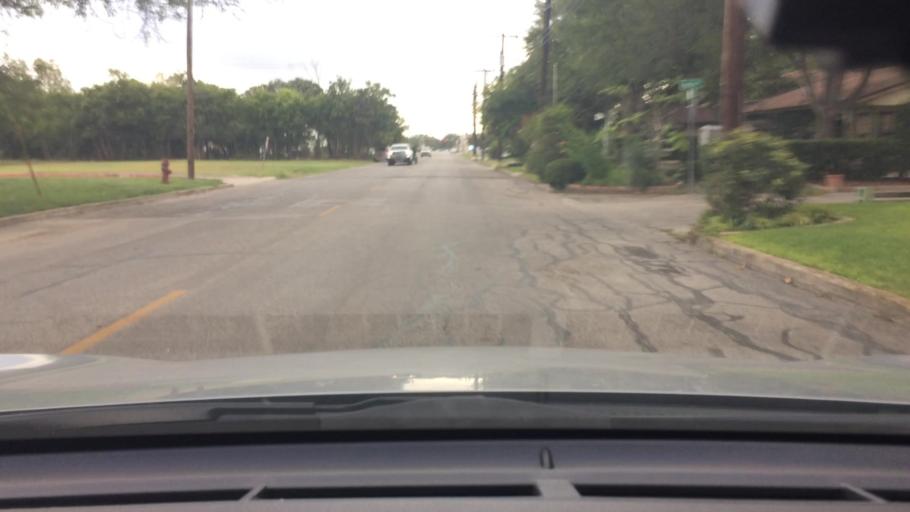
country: US
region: Texas
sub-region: Bexar County
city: Universal City
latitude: 29.5452
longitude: -98.2935
